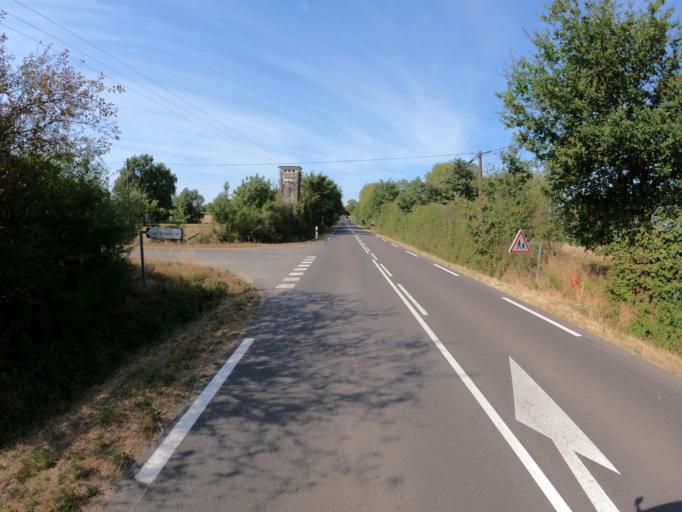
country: FR
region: Pays de la Loire
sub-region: Departement de la Vendee
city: Saint-Christophe-du-Ligneron
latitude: 46.8063
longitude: -1.7781
